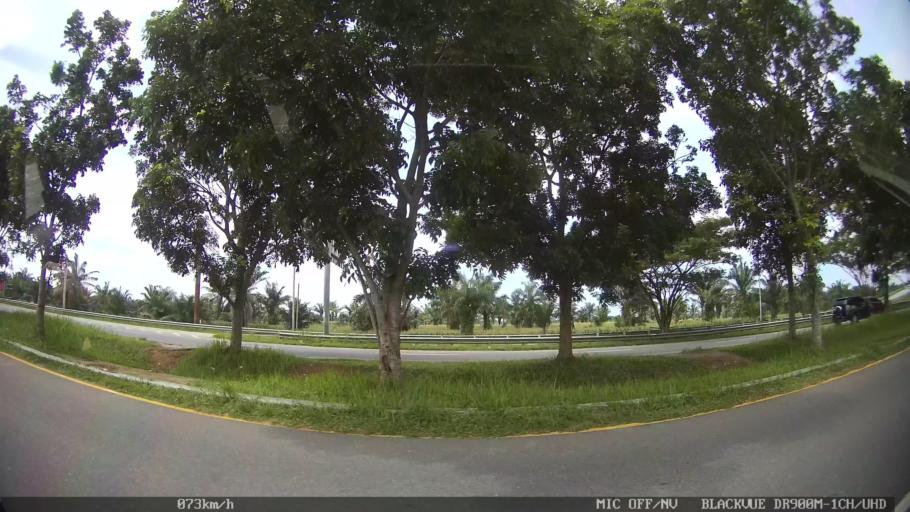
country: ID
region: North Sumatra
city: Percut
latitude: 3.5988
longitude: 98.8392
